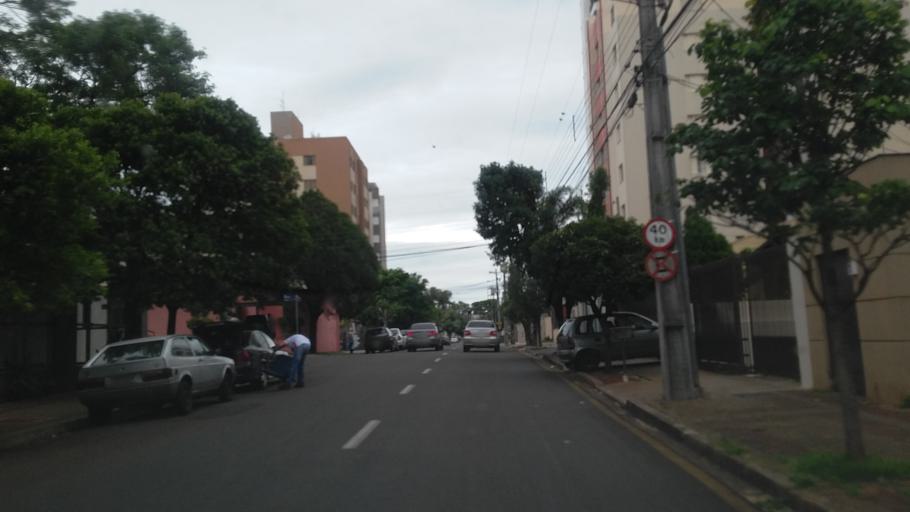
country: BR
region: Parana
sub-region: Londrina
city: Londrina
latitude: -23.3096
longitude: -51.1791
